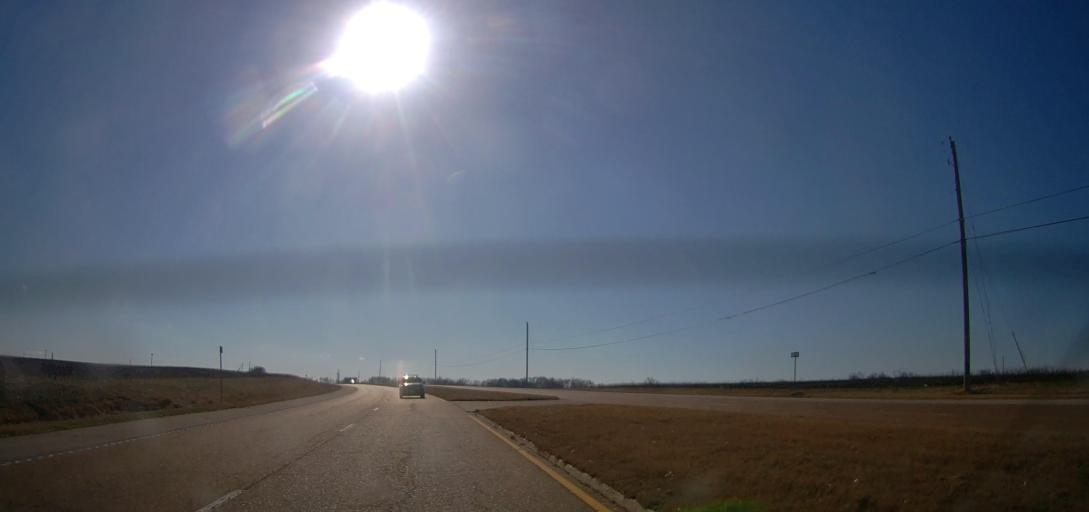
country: US
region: Tennessee
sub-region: Shelby County
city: Millington
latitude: 35.3099
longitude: -89.8810
